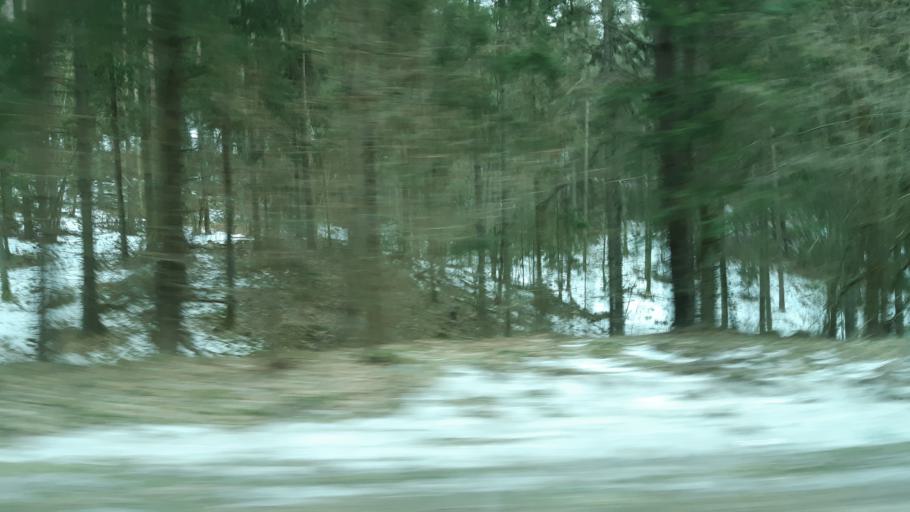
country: PL
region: Podlasie
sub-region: Suwalki
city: Suwalki
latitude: 54.2908
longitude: 22.9556
